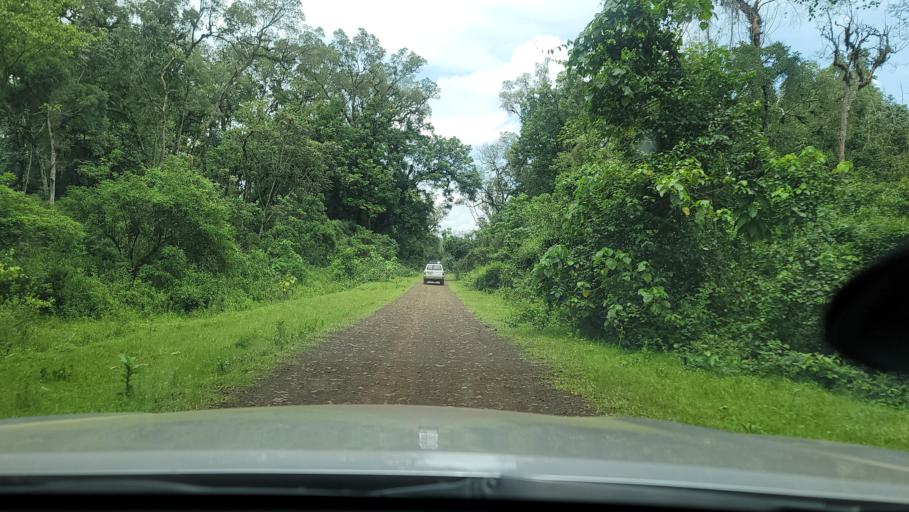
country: ET
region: Southern Nations, Nationalities, and People's Region
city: Bonga
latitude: 7.6526
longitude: 36.2465
